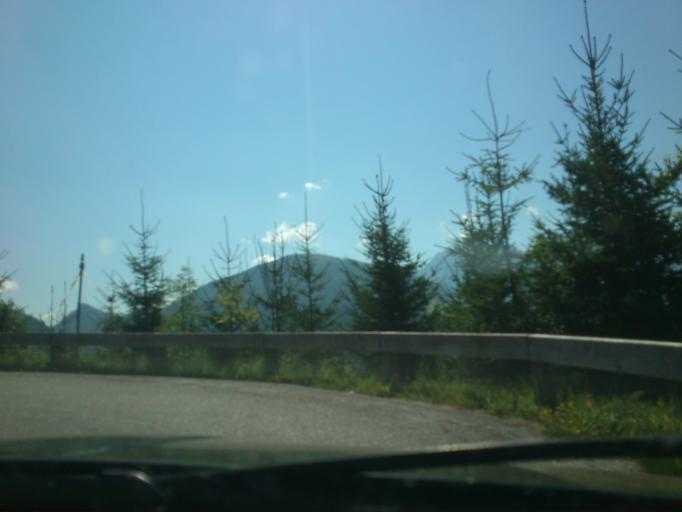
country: AT
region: Upper Austria
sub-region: Politischer Bezirk Kirchdorf an der Krems
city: Rossleithen
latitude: 47.7227
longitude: 14.3617
